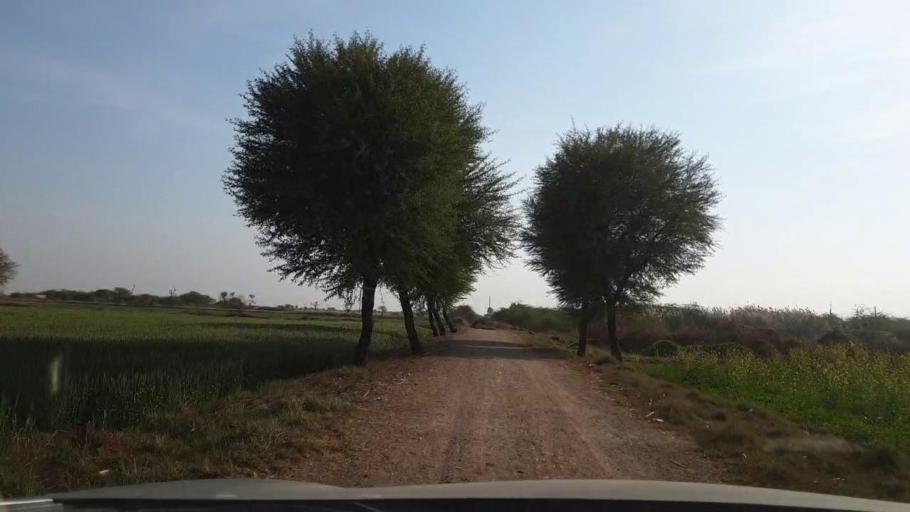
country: PK
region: Sindh
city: Berani
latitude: 25.7147
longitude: 68.8046
